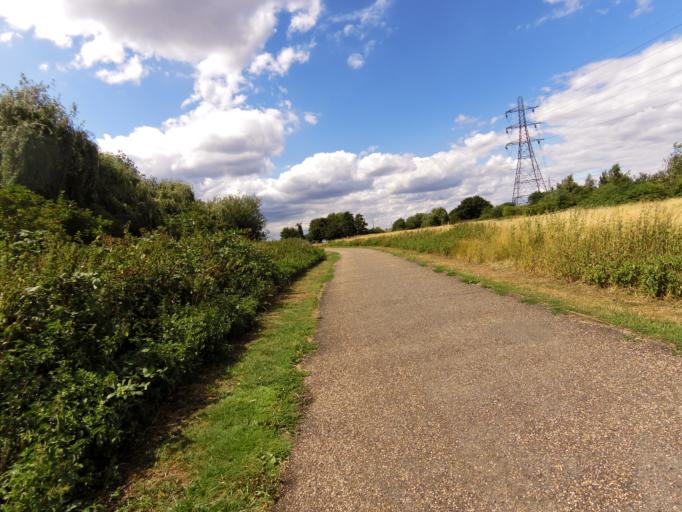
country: GB
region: England
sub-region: Greater London
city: Hackney
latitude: 51.5741
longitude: -0.0516
